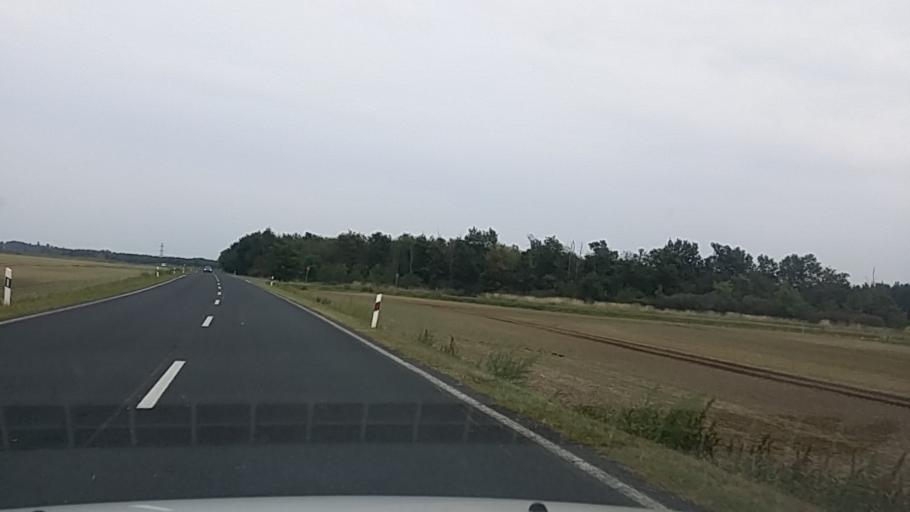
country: HU
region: Vas
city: Vep
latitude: 47.2894
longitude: 16.8144
